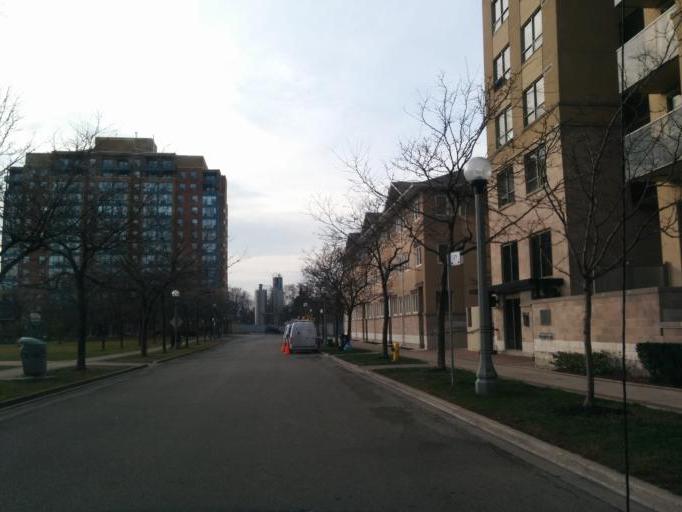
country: CA
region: Ontario
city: Etobicoke
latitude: 43.6013
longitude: -79.5098
